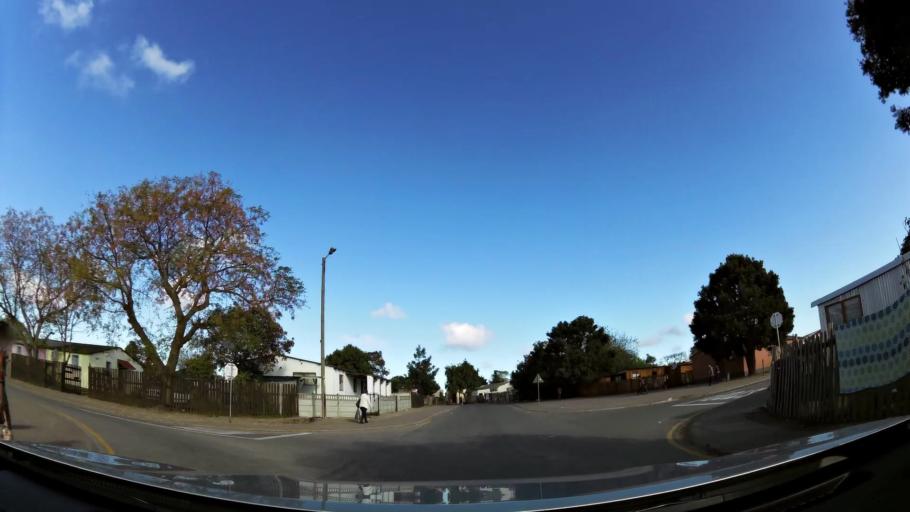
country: ZA
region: Western Cape
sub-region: Eden District Municipality
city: George
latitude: -33.9850
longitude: 22.4762
